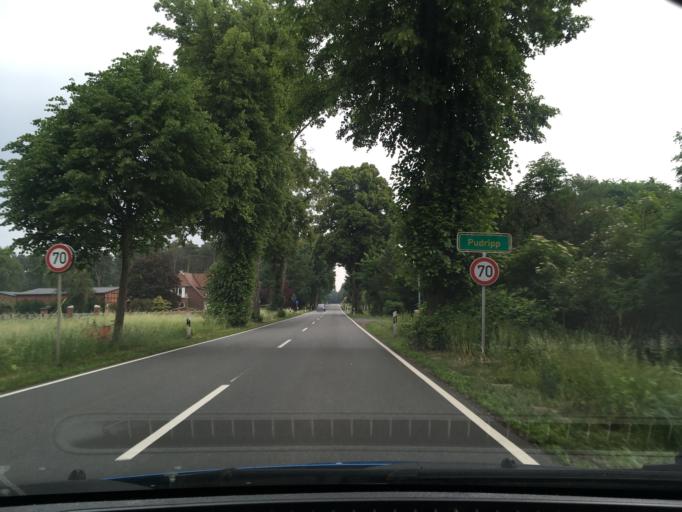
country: DE
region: Lower Saxony
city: Zernien
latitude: 53.0739
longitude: 10.9386
